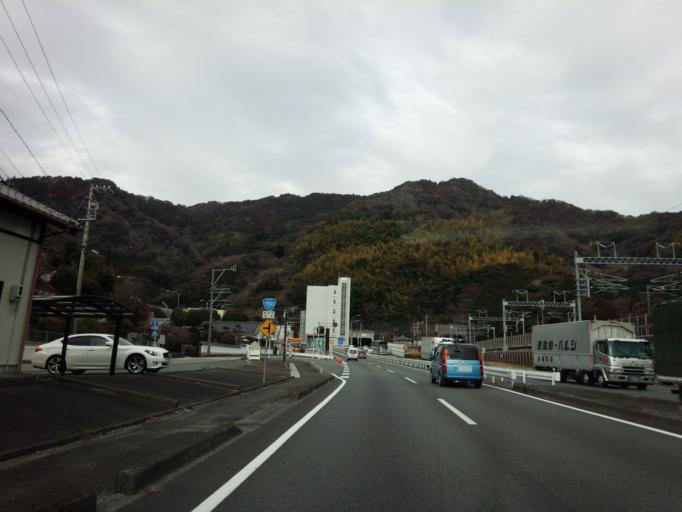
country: JP
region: Shizuoka
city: Yaizu
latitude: 34.8958
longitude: 138.3342
